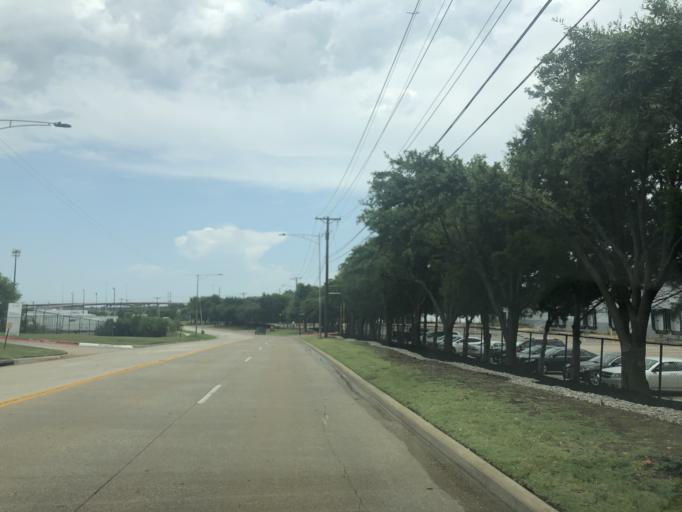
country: US
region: Texas
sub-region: Dallas County
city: Grand Prairie
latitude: 32.7564
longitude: -97.0411
